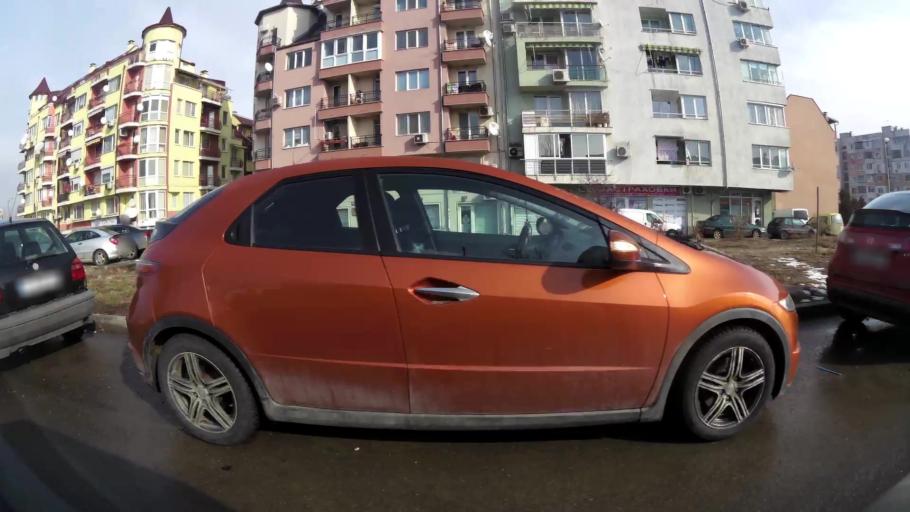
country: BG
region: Sofiya
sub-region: Obshtina Bozhurishte
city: Bozhurishte
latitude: 42.7204
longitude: 23.2567
